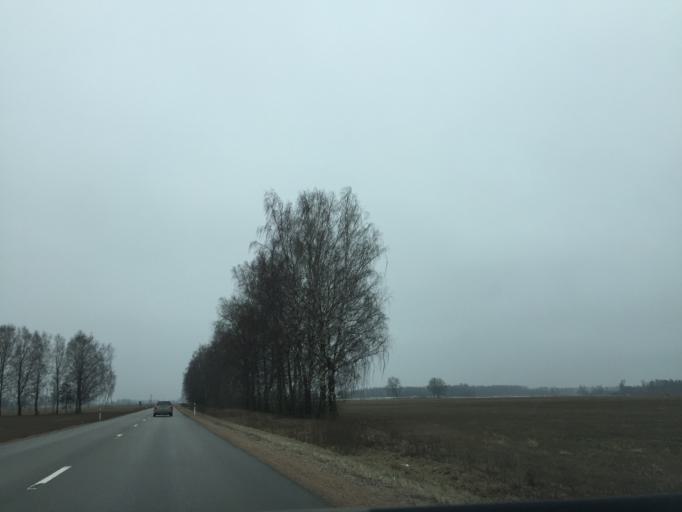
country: LV
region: Lecava
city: Iecava
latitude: 56.6006
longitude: 24.0964
